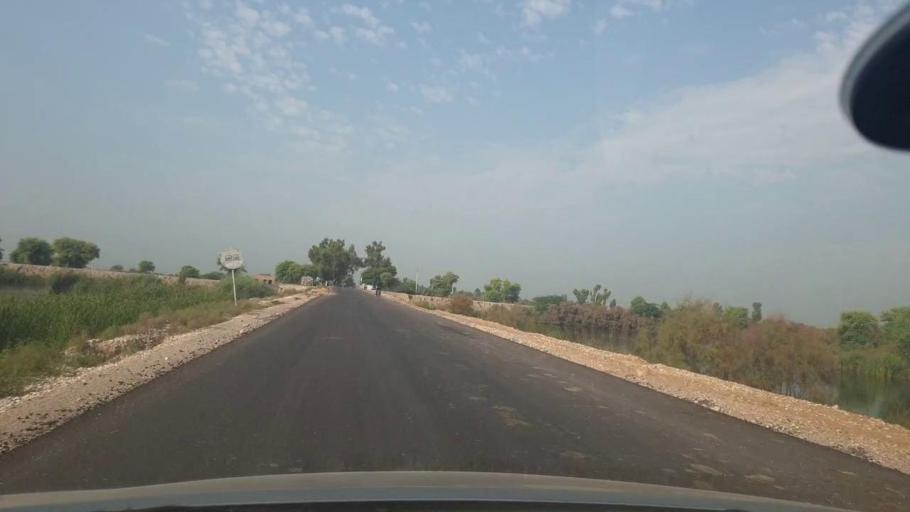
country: PK
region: Sindh
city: Jacobabad
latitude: 28.0925
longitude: 68.3273
